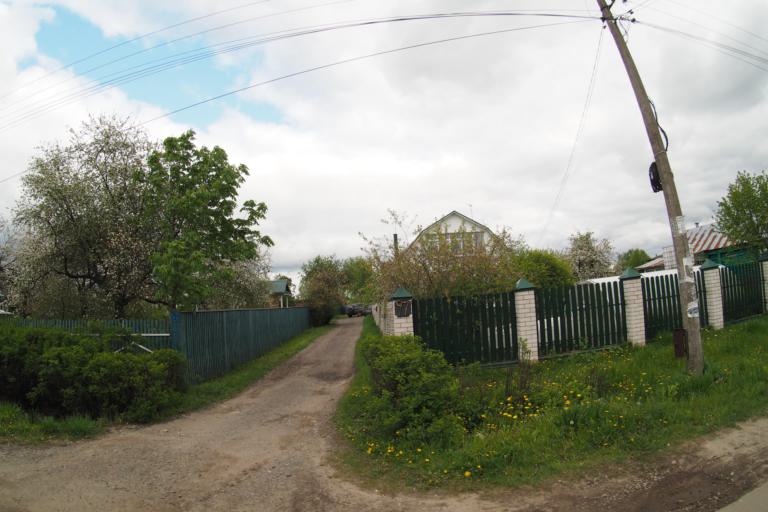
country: RU
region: Moskovskaya
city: Rechitsy
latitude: 55.5822
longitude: 38.5060
